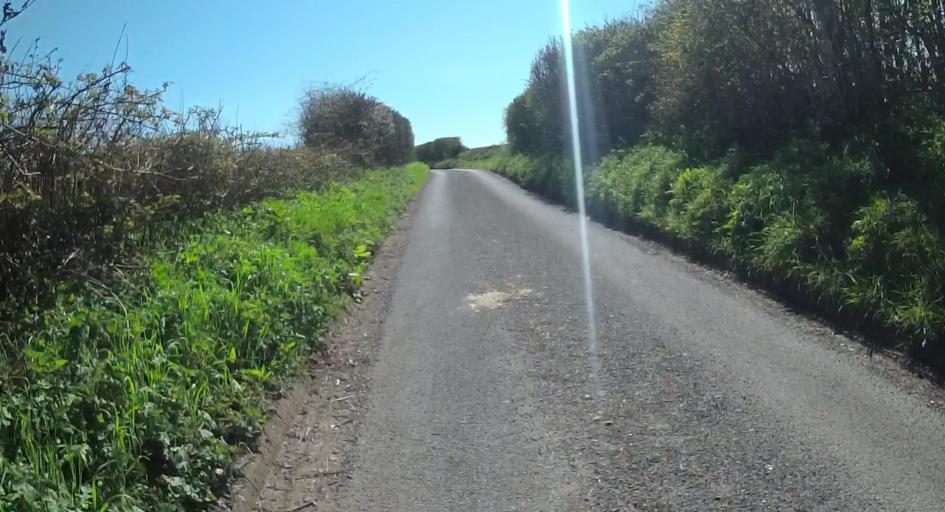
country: GB
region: England
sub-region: Hampshire
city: Odiham
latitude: 51.2441
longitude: -0.9028
